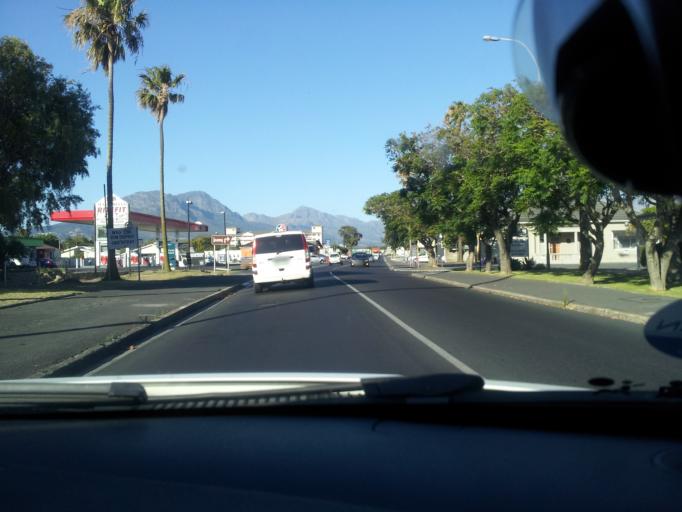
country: ZA
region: Western Cape
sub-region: Cape Winelands District Municipality
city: Stellenbosch
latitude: -34.1113
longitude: 18.8347
